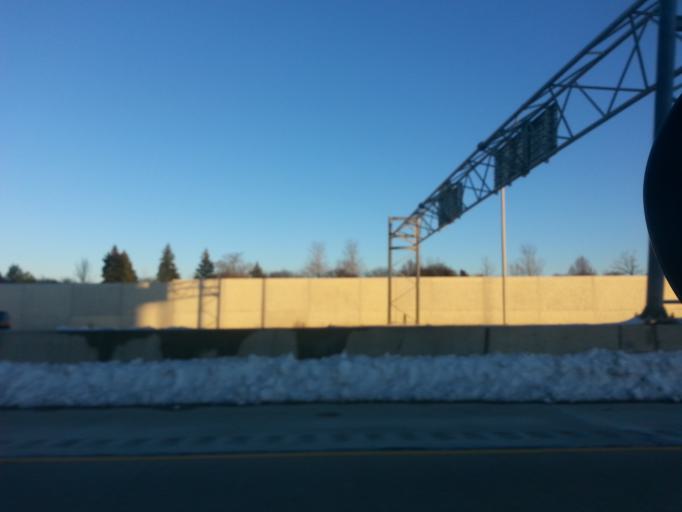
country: US
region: Illinois
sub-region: Cook County
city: Northbrook
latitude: 42.1020
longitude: -87.8682
